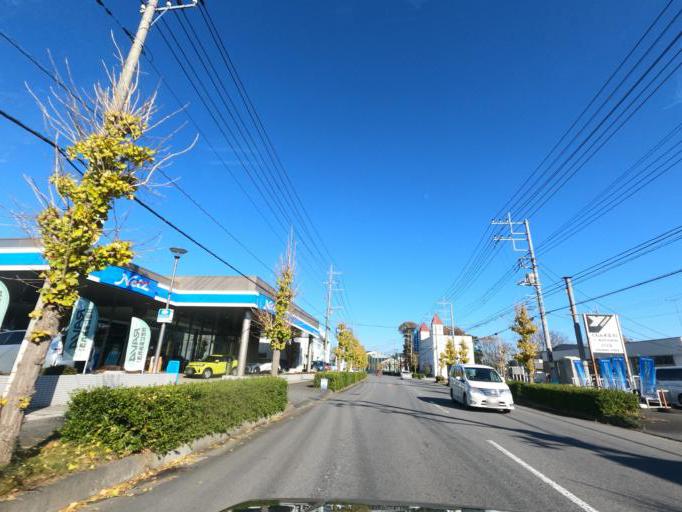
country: JP
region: Ibaraki
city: Mitsukaido
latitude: 35.9789
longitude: 139.9754
